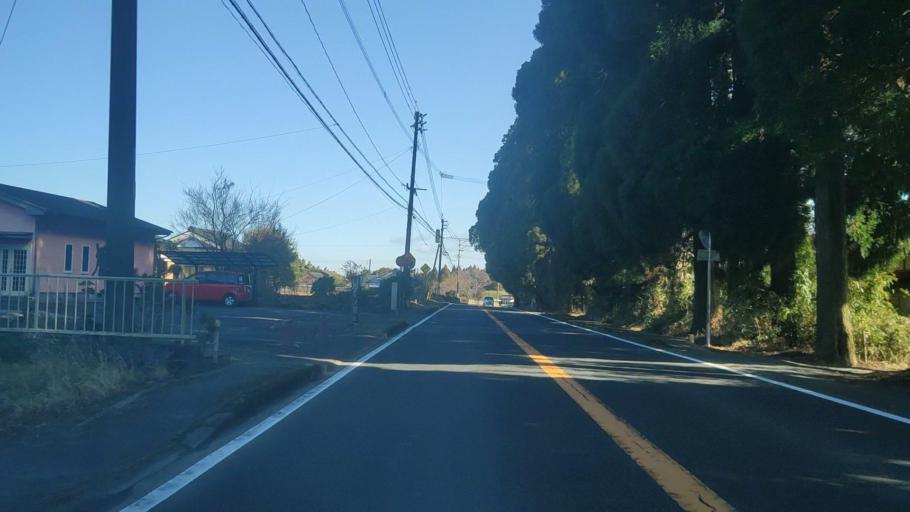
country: JP
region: Kagoshima
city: Sueyoshicho-ninokata
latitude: 31.6854
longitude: 130.9446
